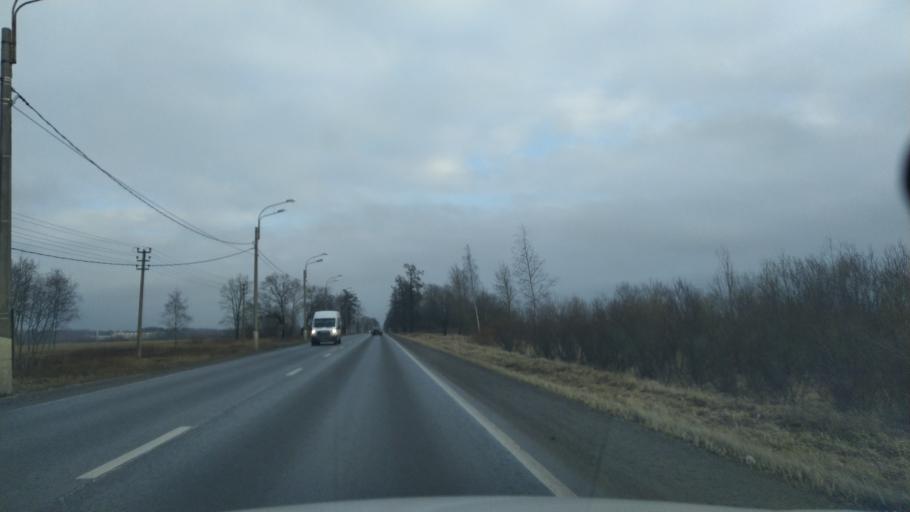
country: RU
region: St.-Petersburg
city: Aleksandrovskaya
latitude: 59.7106
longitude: 30.3179
